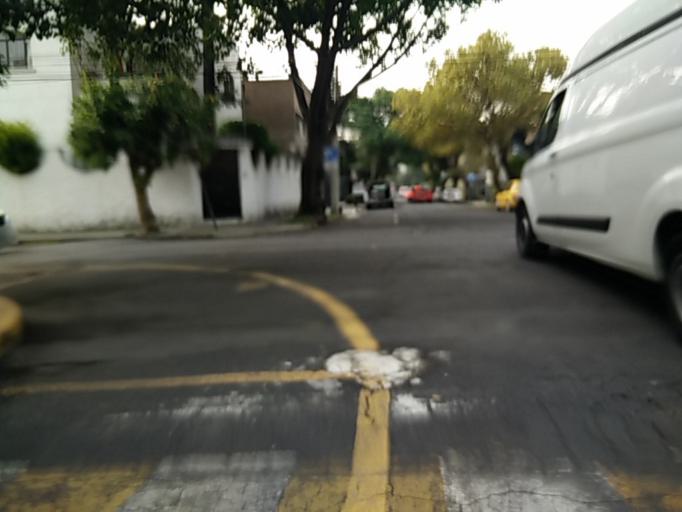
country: MX
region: Mexico City
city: Miguel Hidalgo
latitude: 19.4327
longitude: -99.1802
